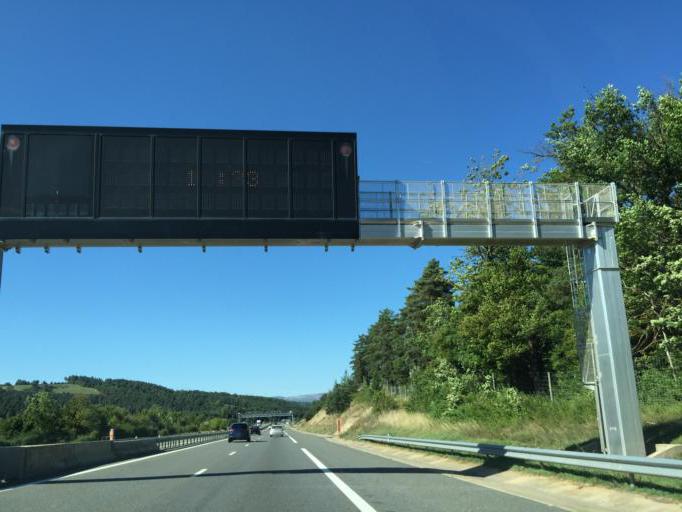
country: FR
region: Midi-Pyrenees
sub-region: Departement de l'Aveyron
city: Severac-le-Chateau
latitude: 44.3674
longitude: 3.1162
